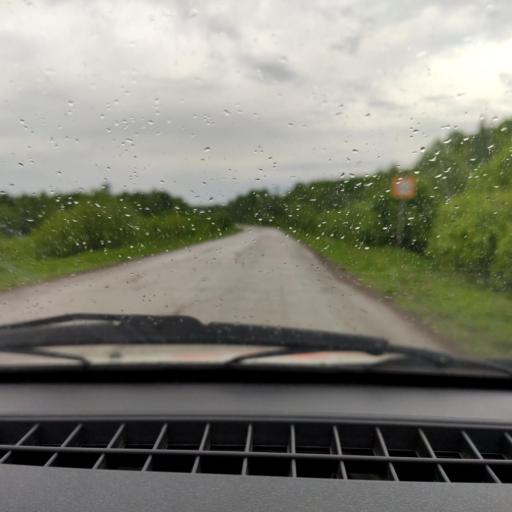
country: RU
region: Bashkortostan
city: Kudeyevskiy
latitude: 54.8527
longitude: 56.8170
